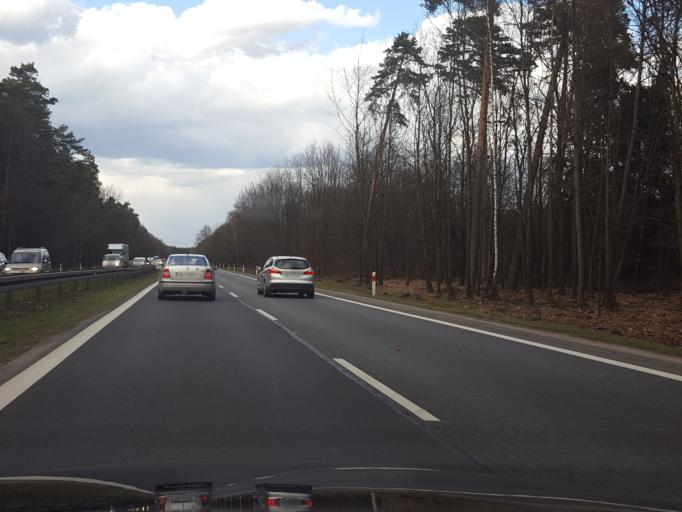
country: PL
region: Silesian Voivodeship
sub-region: Powiat pszczynski
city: Kobior
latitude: 50.0368
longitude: 18.9417
